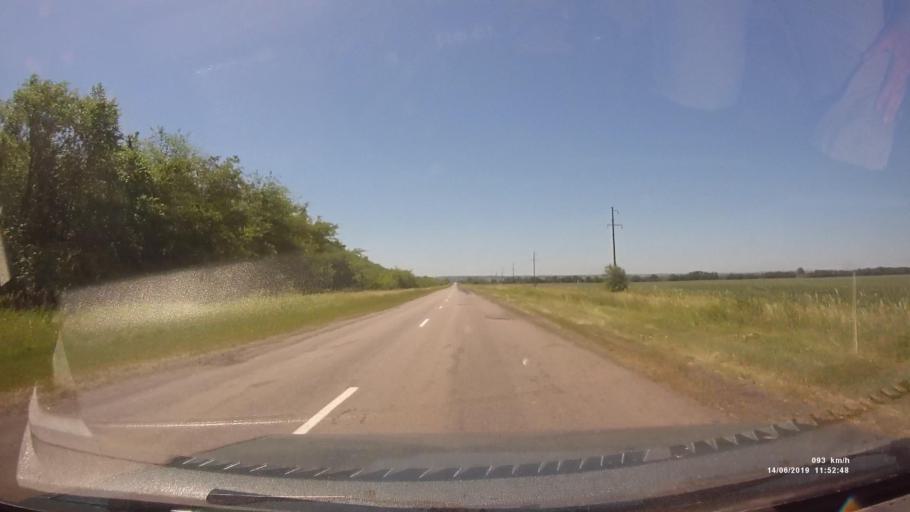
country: RU
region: Rostov
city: Kazanskaya
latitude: 49.8330
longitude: 41.2222
